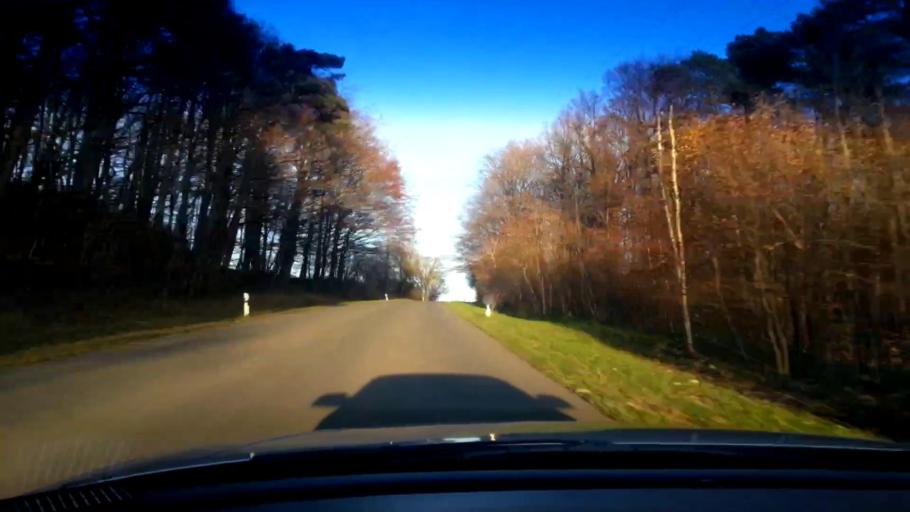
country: DE
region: Bavaria
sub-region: Upper Franconia
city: Rattelsdorf
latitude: 50.0595
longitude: 10.8930
